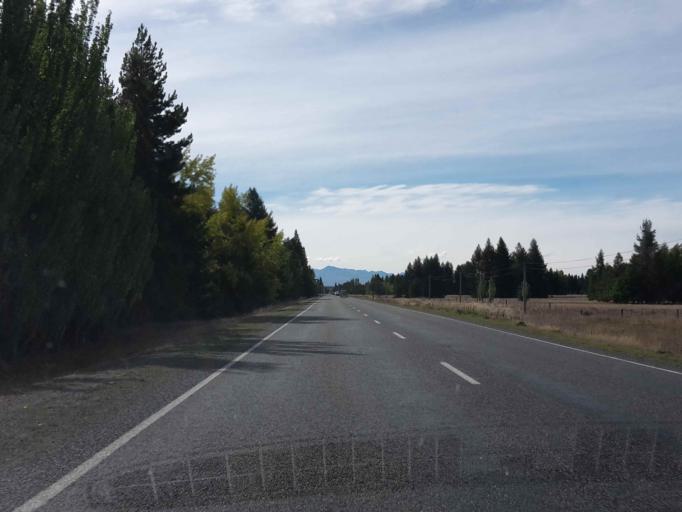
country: NZ
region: Canterbury
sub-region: Timaru District
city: Pleasant Point
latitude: -44.2709
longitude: 170.1003
